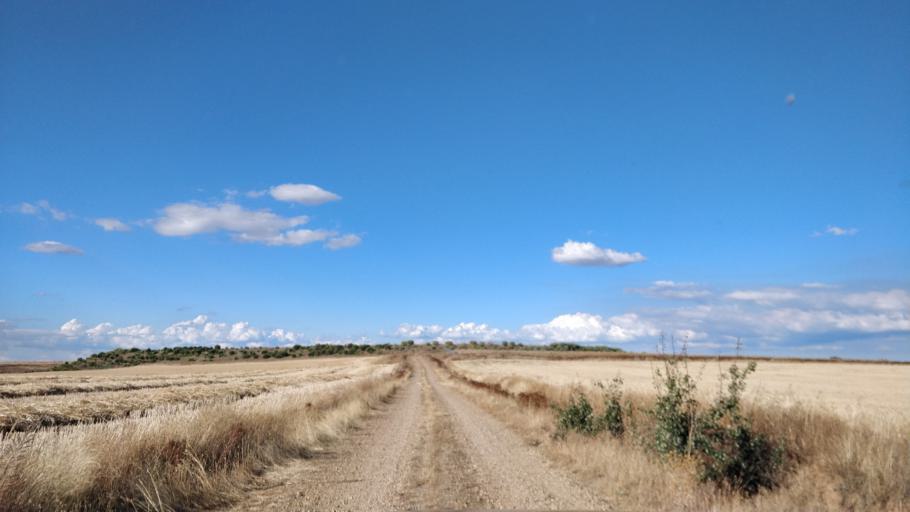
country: ES
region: Castille and Leon
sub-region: Provincia de Leon
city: Santa Cristina de Valmadrigal
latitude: 42.3432
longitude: -5.2694
